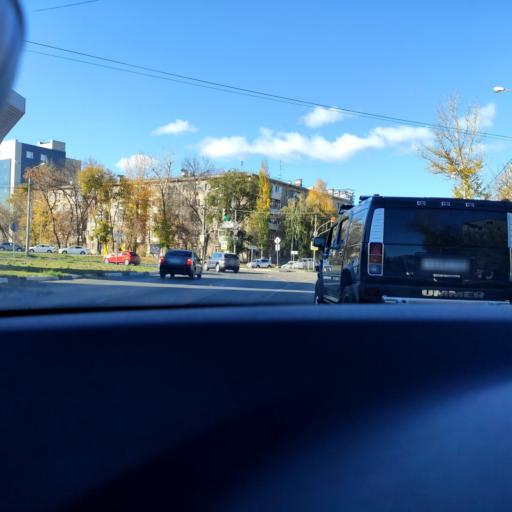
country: RU
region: Samara
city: Samara
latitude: 53.2001
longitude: 50.1645
